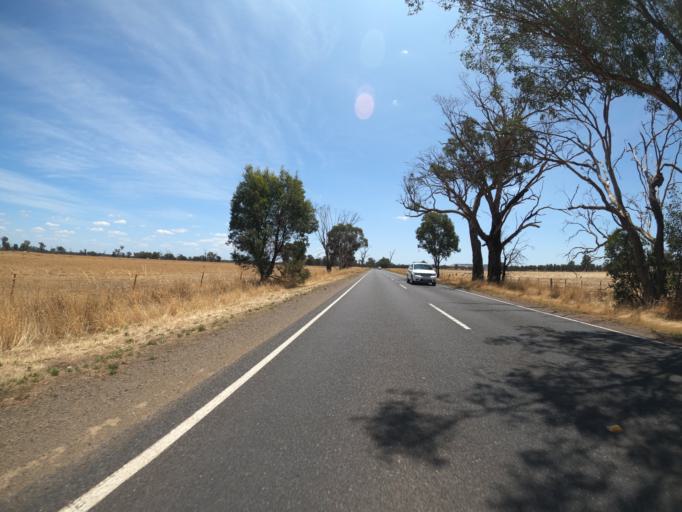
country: AU
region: Victoria
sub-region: Benalla
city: Benalla
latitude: -36.5131
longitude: 146.0301
